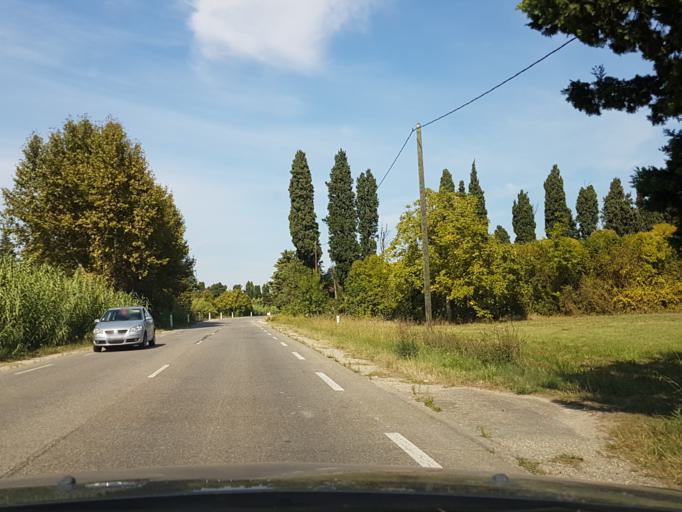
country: FR
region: Provence-Alpes-Cote d'Azur
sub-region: Departement des Bouches-du-Rhone
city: Noves
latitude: 43.8664
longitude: 4.8990
